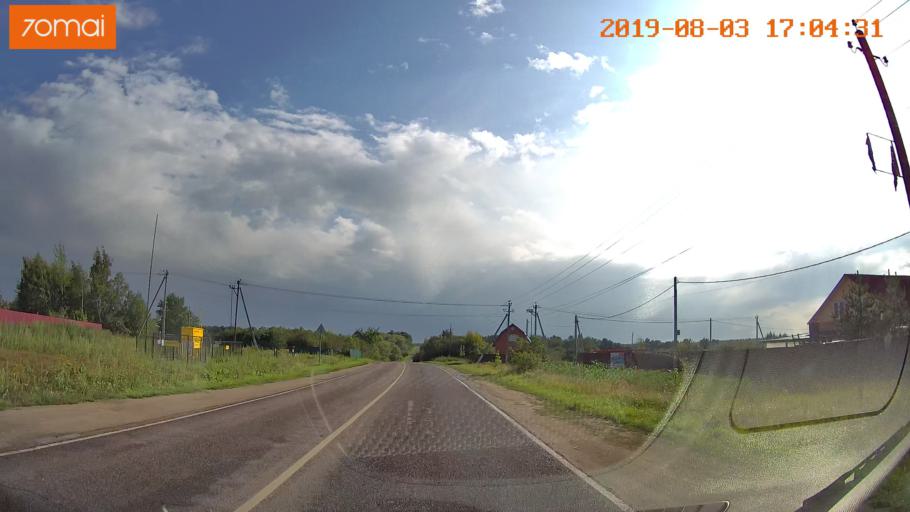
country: RU
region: Moskovskaya
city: Troitskoye
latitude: 55.3281
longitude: 38.5576
